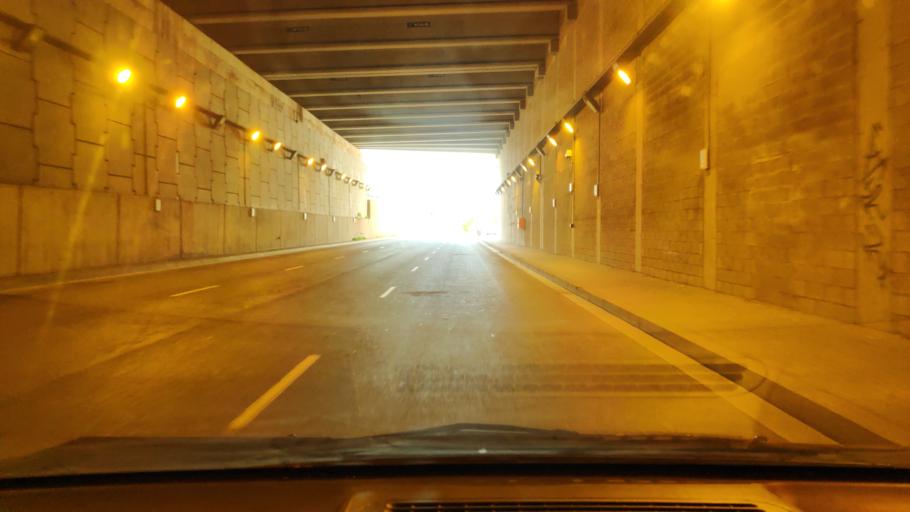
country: ES
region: Catalonia
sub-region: Provincia de Barcelona
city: Sant Adria de Besos
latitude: 41.4119
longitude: 2.2230
